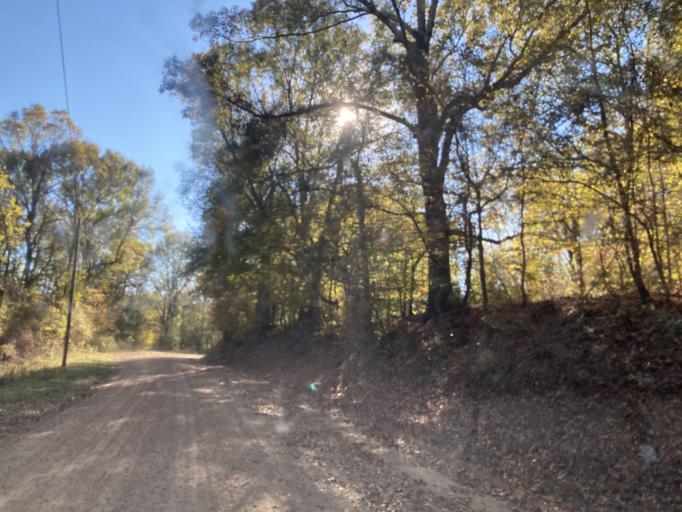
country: US
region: Mississippi
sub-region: Yazoo County
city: Yazoo City
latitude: 32.7436
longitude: -90.4336
